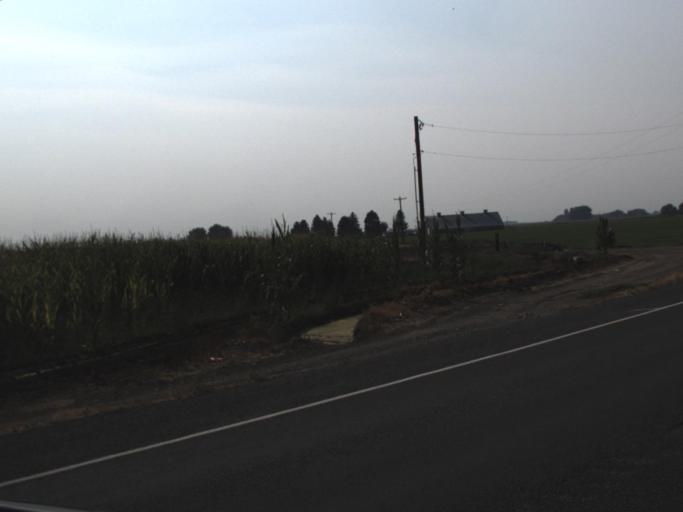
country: US
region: Washington
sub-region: Yakima County
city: Toppenish
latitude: 46.3382
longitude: -120.2617
